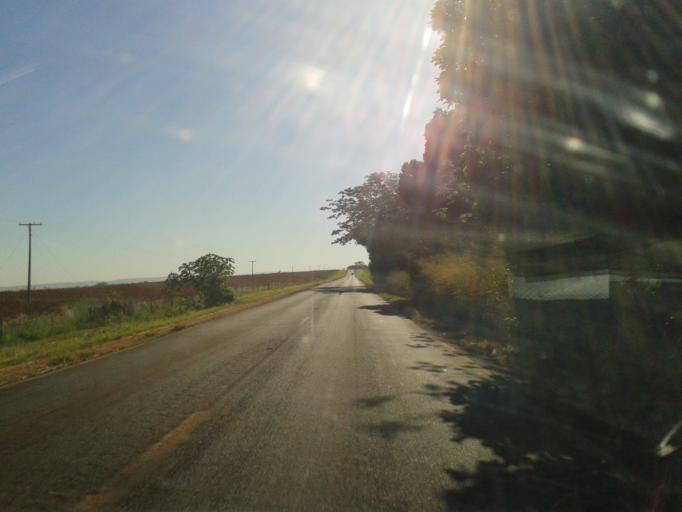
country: BR
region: Minas Gerais
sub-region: Capinopolis
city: Capinopolis
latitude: -18.5879
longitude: -49.5150
